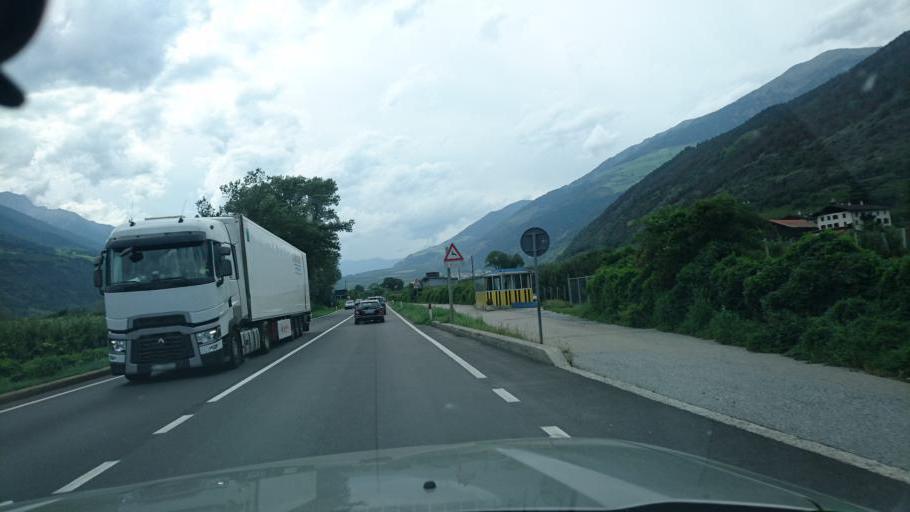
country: IT
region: Trentino-Alto Adige
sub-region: Bolzano
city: Silandro
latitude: 46.6231
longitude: 10.8060
